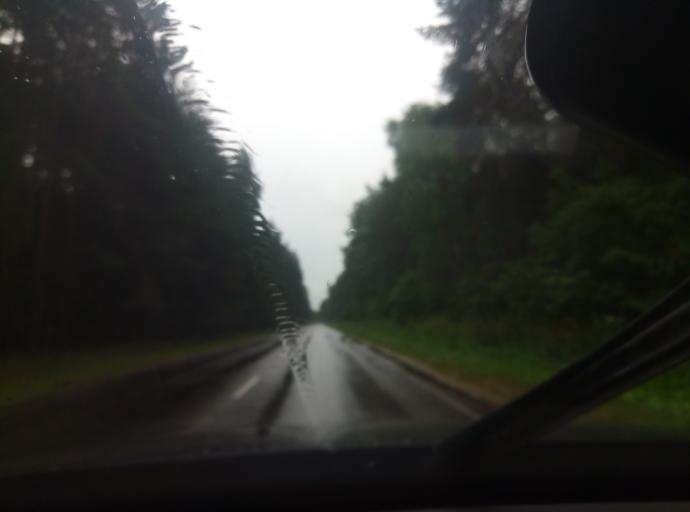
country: RU
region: Kaluga
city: Vysokinichi
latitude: 54.9410
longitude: 36.8422
